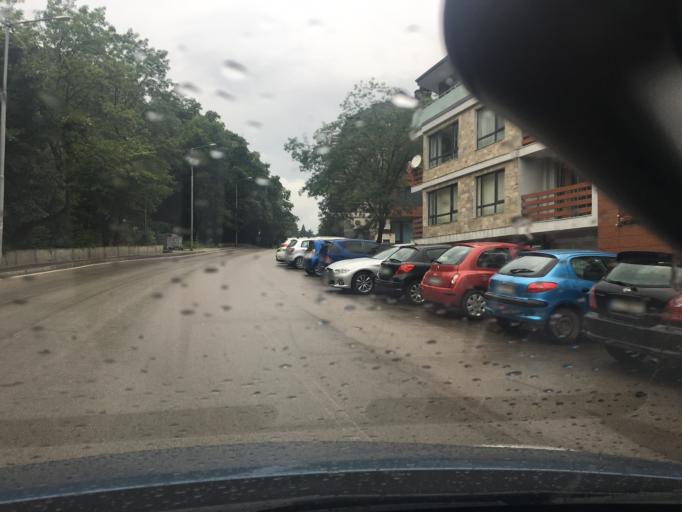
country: BG
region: Sofia-Capital
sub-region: Stolichna Obshtina
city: Sofia
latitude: 42.6426
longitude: 23.2851
